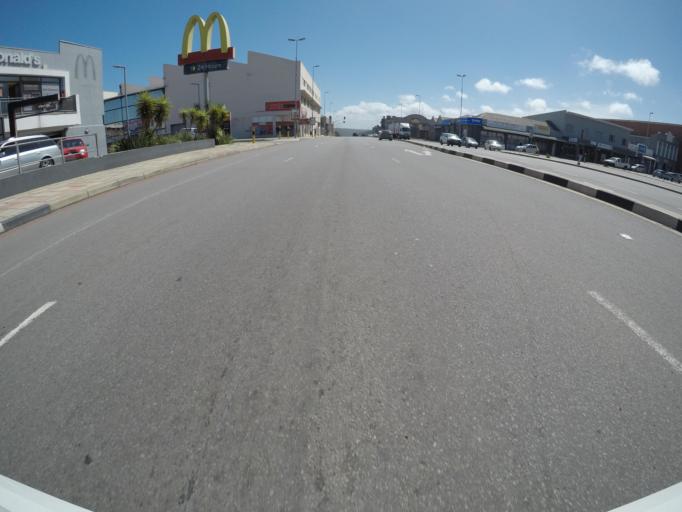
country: ZA
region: Eastern Cape
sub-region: Buffalo City Metropolitan Municipality
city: East London
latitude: -33.0196
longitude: 27.9053
